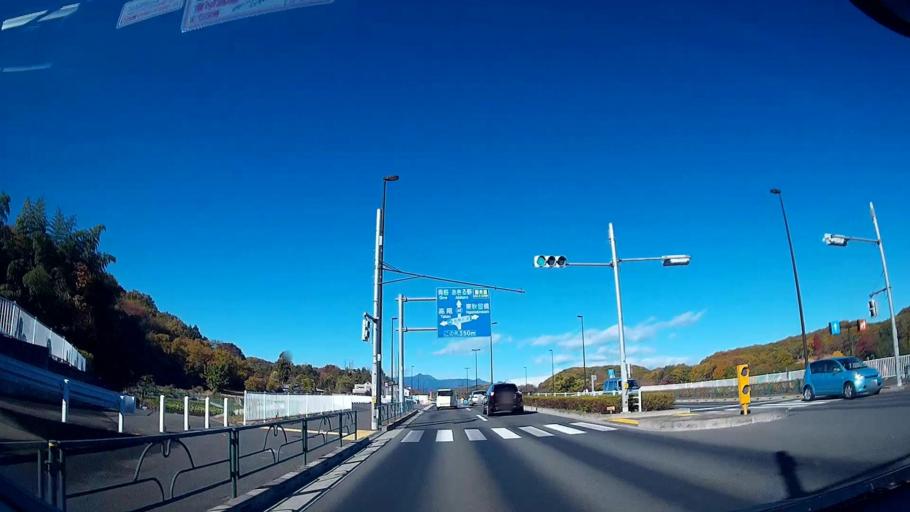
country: JP
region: Tokyo
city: Fussa
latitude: 35.7050
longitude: 139.3003
